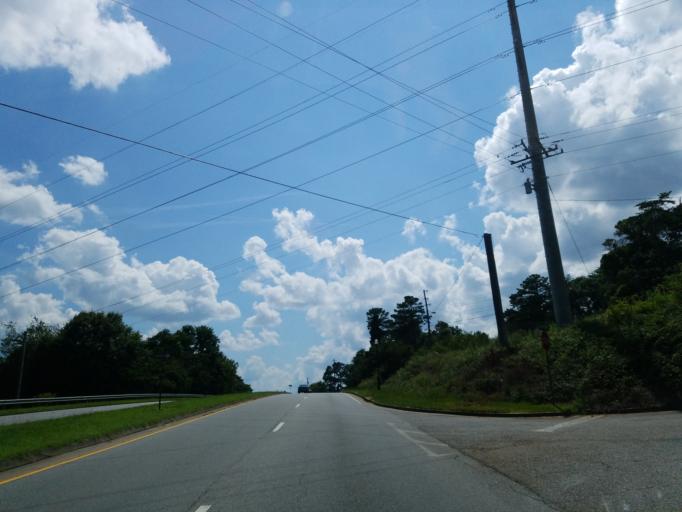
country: US
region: Georgia
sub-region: Forsyth County
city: Cumming
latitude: 34.2083
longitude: -84.1279
